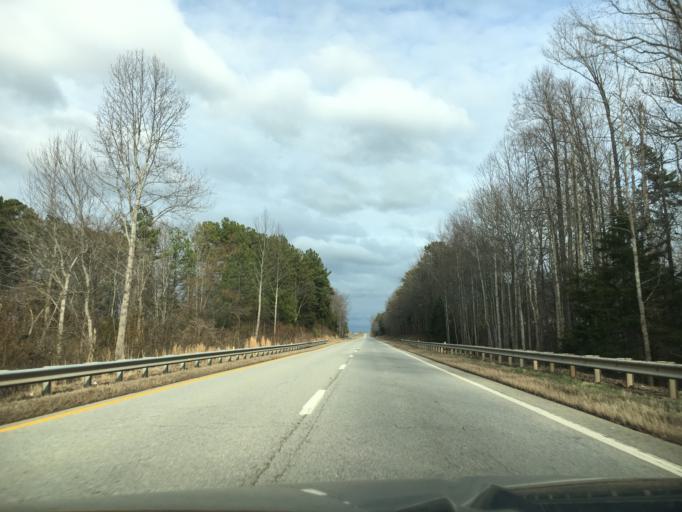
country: US
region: Virginia
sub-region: Lunenburg County
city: Victoria
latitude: 37.1460
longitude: -78.2942
